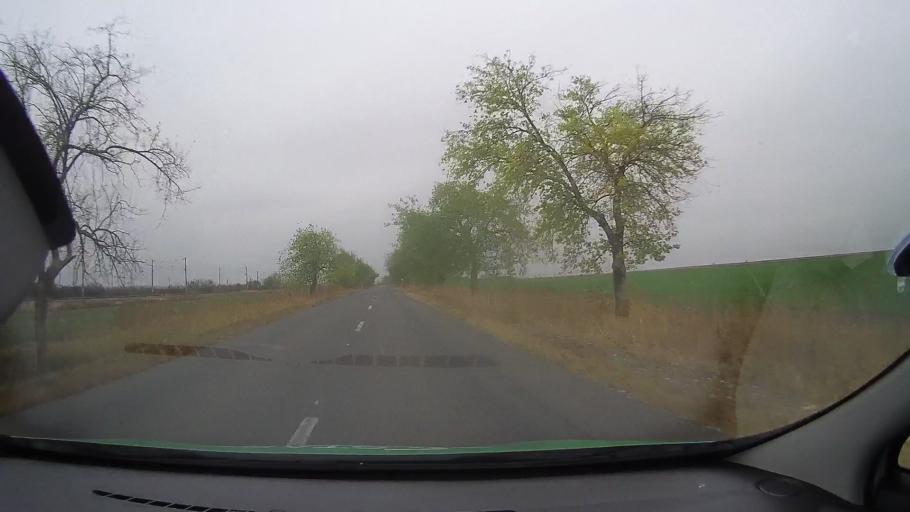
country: RO
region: Ialomita
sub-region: Comuna Valea Ciorii
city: Valea Ciorii
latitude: 44.6953
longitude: 27.6023
